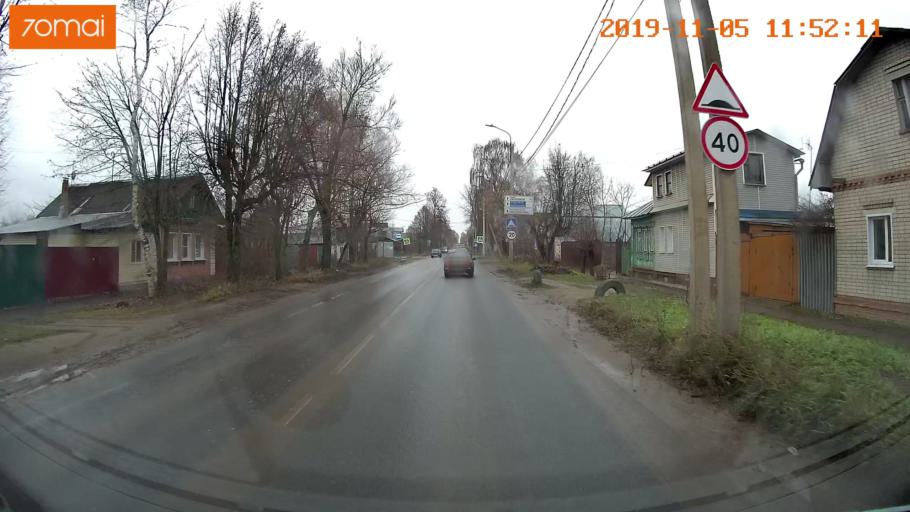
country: RU
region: Ivanovo
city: Bogorodskoye
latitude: 57.0011
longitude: 41.0292
